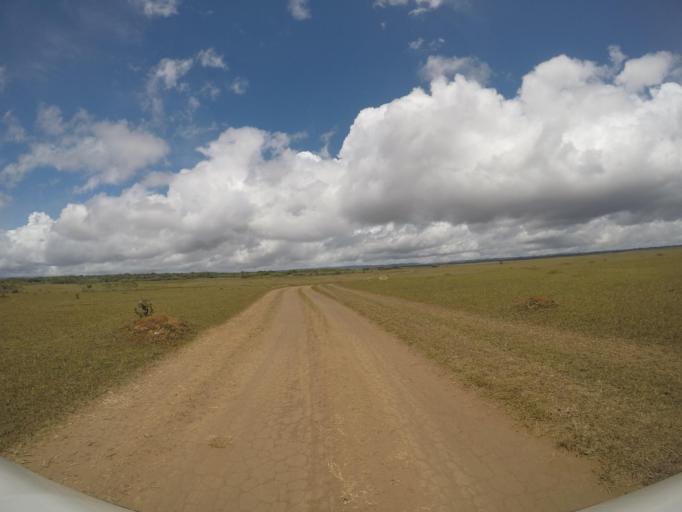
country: TL
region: Lautem
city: Lospalos
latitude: -8.4624
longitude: 126.9845
